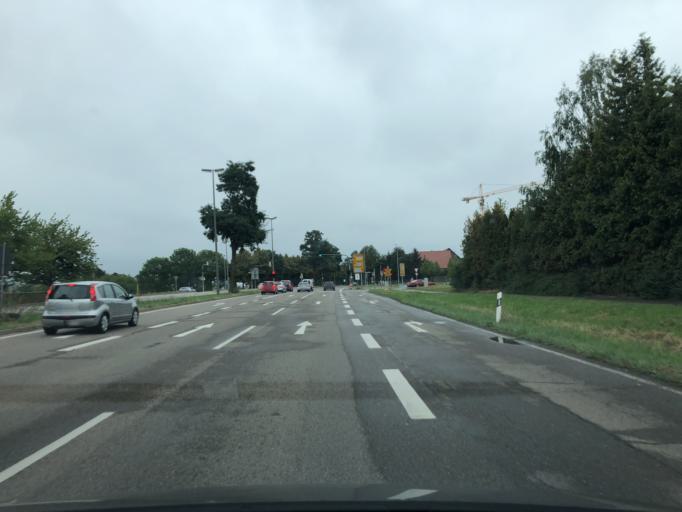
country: DE
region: Baden-Wuerttemberg
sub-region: Regierungsbezirk Stuttgart
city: Magstadt
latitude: 48.7028
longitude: 8.9756
